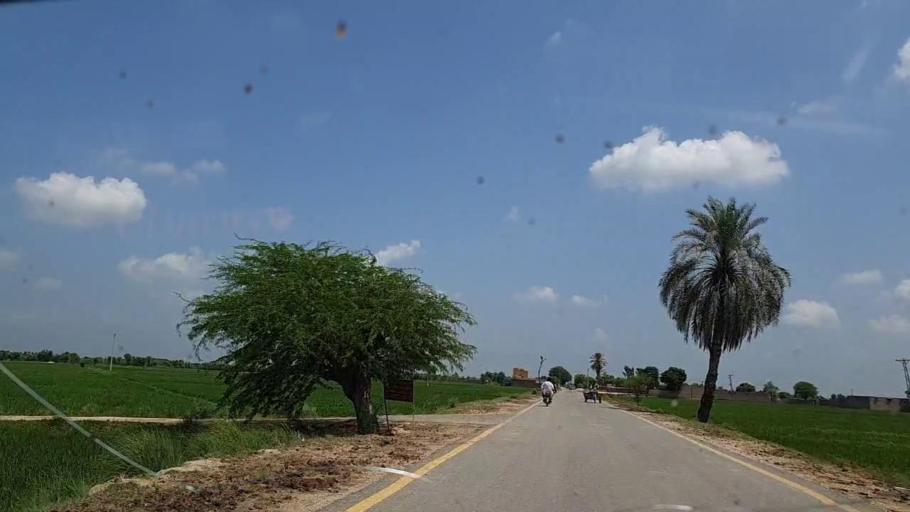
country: PK
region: Sindh
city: Tharu Shah
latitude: 26.9809
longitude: 68.0825
